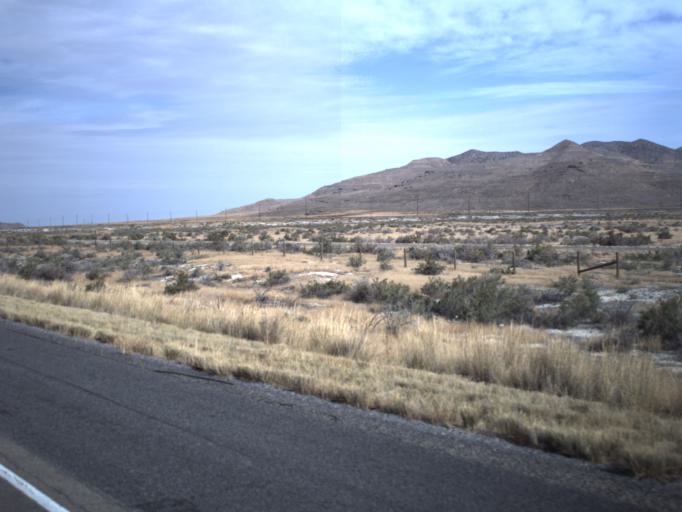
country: US
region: Utah
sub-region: Tooele County
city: Grantsville
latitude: 40.7846
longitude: -112.8208
